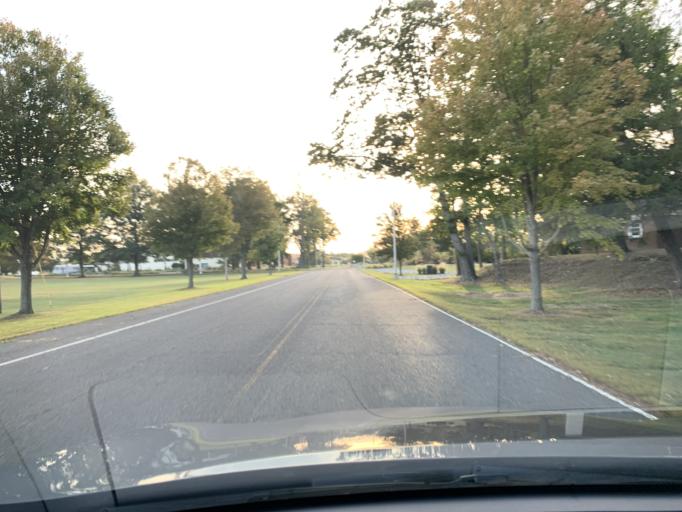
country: US
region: New Jersey
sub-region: Monmouth County
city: Little Silver
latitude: 40.3163
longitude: -74.0420
